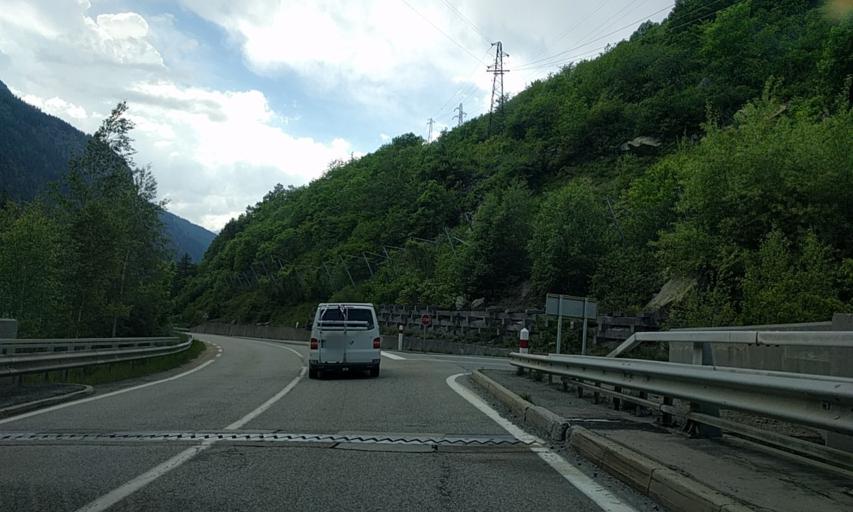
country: FR
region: Rhone-Alpes
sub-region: Departement de la Savoie
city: Saint-Michel-de-Maurienne
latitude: 45.2074
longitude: 6.5641
